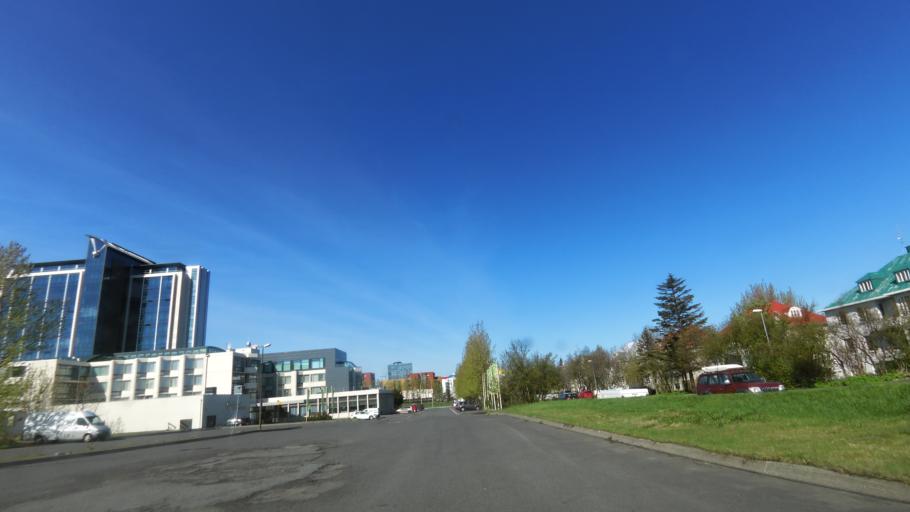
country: IS
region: Capital Region
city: Reykjavik
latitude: 64.1424
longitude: -21.8886
